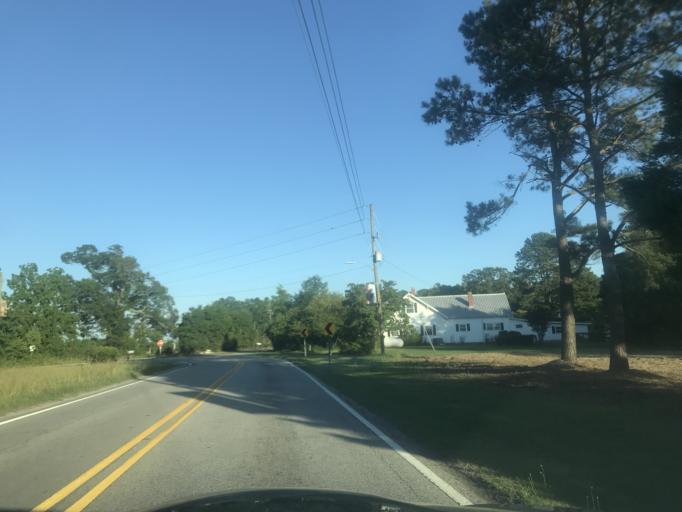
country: US
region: North Carolina
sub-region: Johnston County
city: Archer Lodge
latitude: 35.6934
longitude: -78.3745
